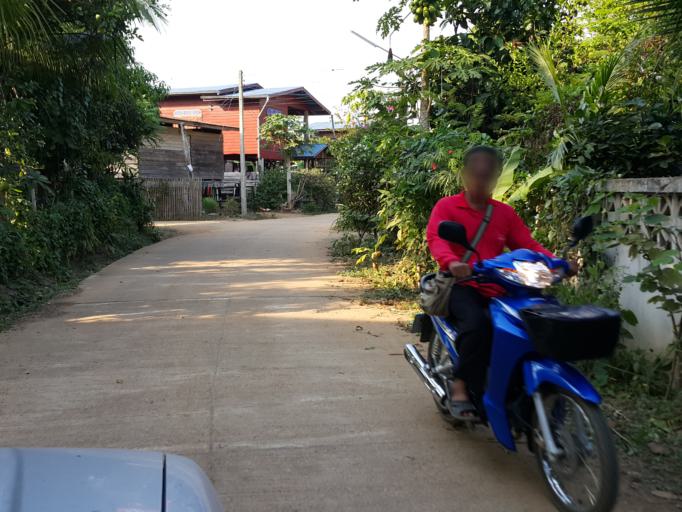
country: TH
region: Sukhothai
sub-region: Amphoe Si Satchanalai
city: Si Satchanalai
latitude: 17.4687
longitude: 99.6495
